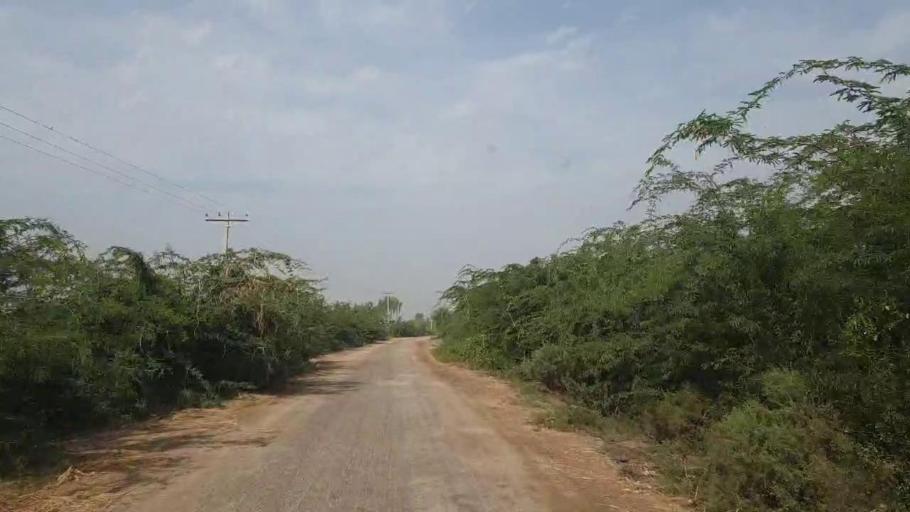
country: PK
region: Sindh
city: Tando Bago
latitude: 24.9210
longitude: 68.9919
